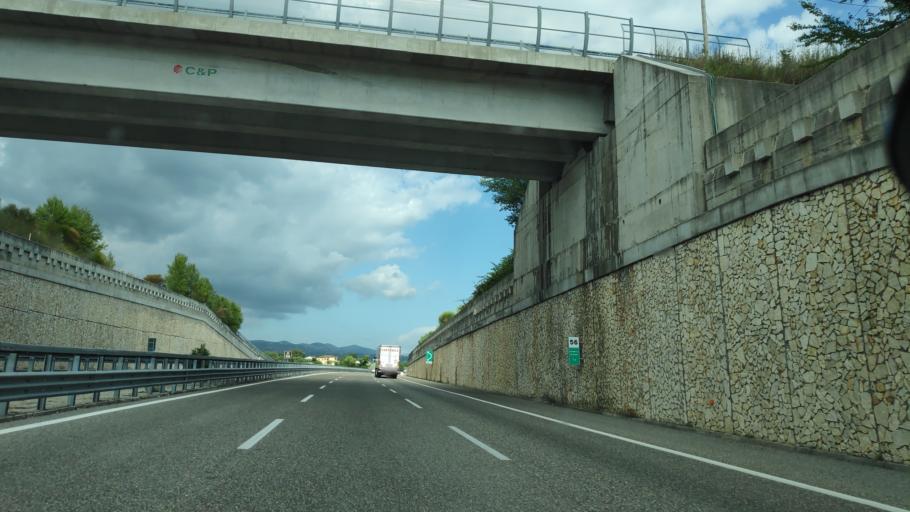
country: IT
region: Campania
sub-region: Provincia di Salerno
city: Contursi Terme
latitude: 40.6136
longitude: 15.2684
